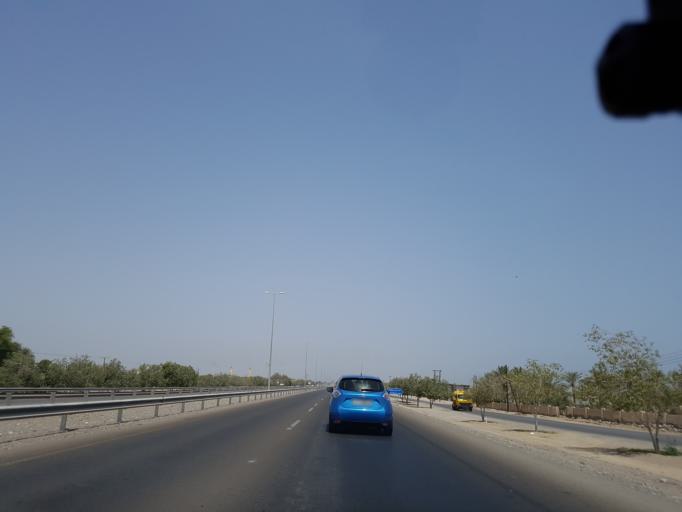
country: OM
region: Al Batinah
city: Saham
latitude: 24.2122
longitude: 56.8458
